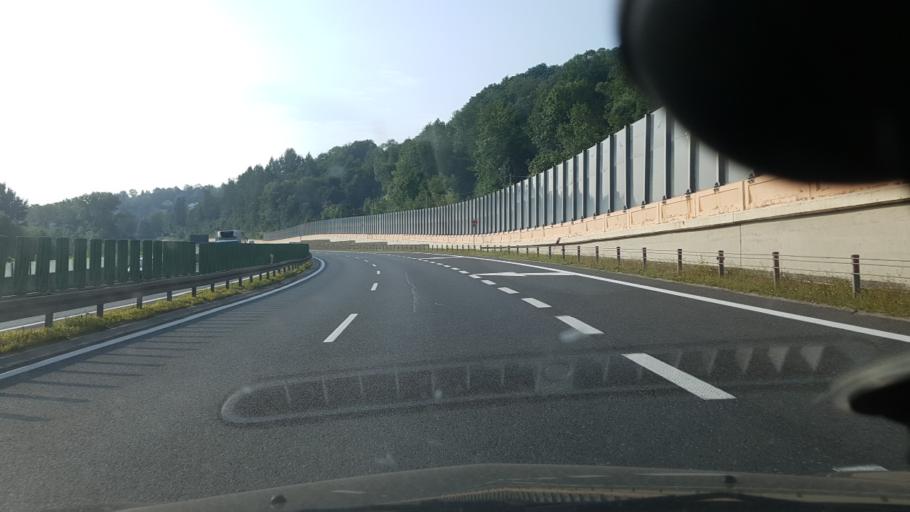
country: PL
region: Lesser Poland Voivodeship
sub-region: Powiat myslenicki
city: Stroza
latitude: 49.7924
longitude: 19.9250
